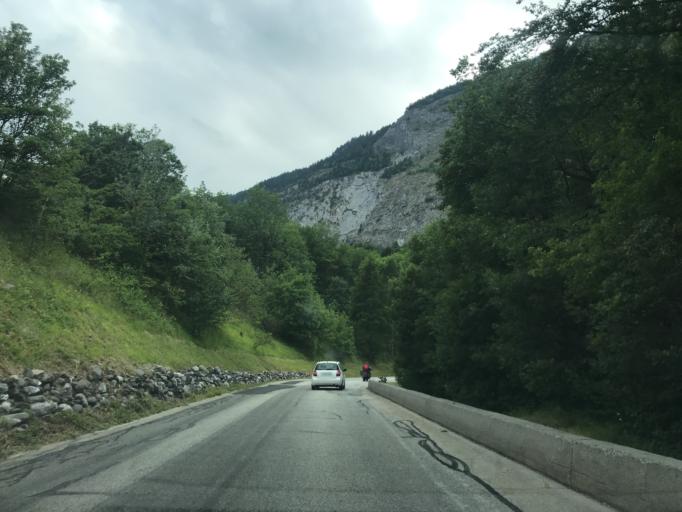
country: FR
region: Rhone-Alpes
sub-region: Departement de la Savoie
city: Saint-Michel-de-Maurienne
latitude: 45.2106
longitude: 6.4573
